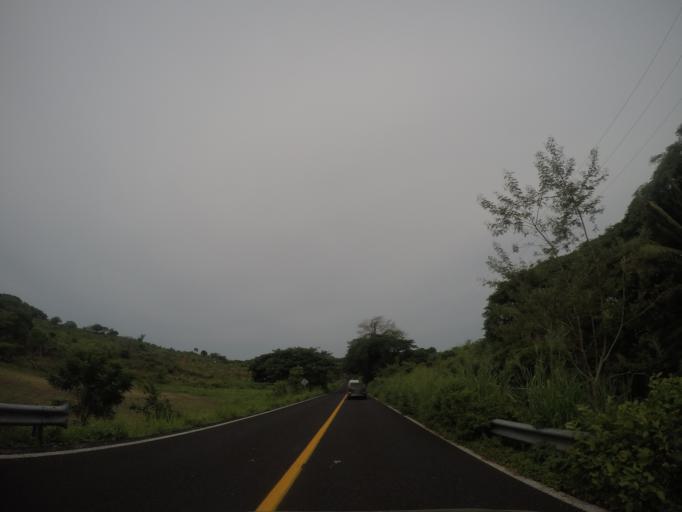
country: MX
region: Oaxaca
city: San Pedro Mixtepec
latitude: 15.9511
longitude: -97.2759
